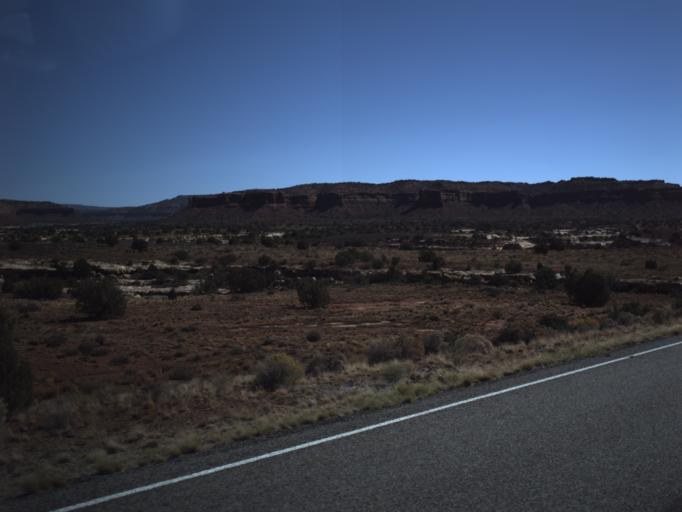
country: US
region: Utah
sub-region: San Juan County
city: Blanding
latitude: 37.7027
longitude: -110.2364
